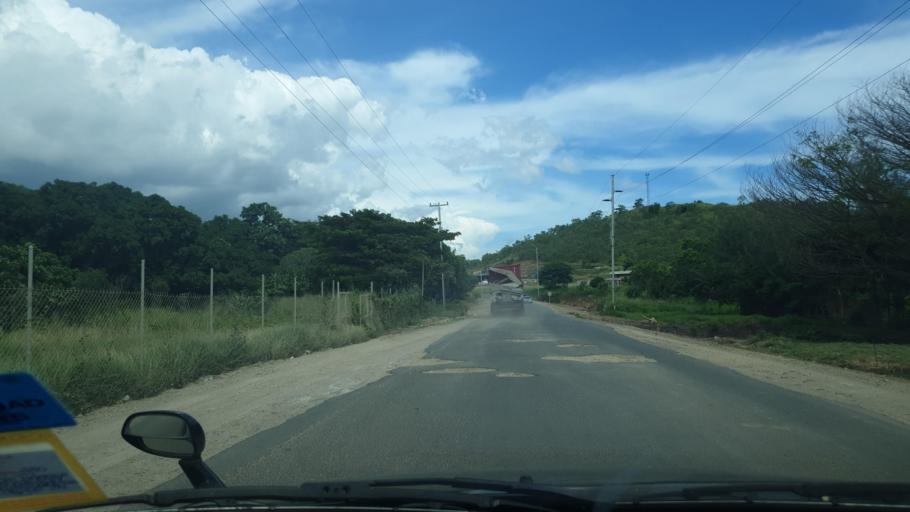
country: PG
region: National Capital
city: Port Moresby
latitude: -9.4166
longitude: 147.1162
